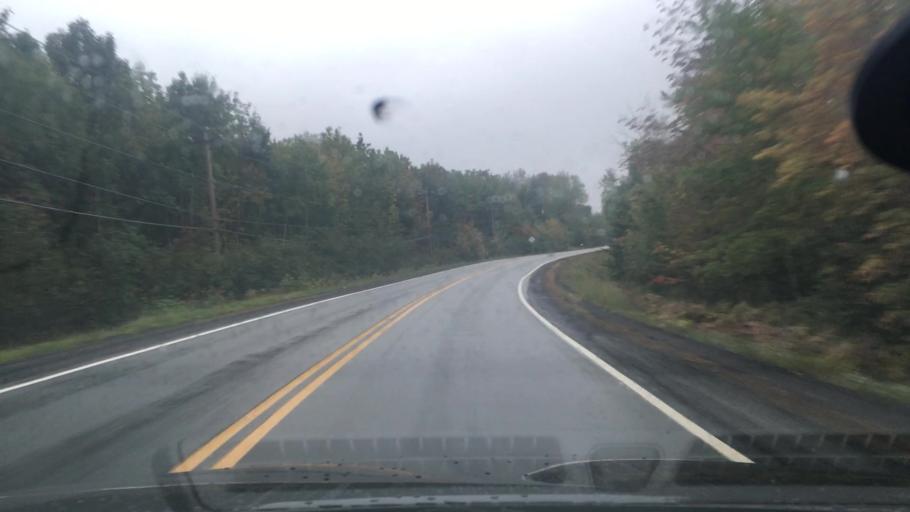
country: CA
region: Nova Scotia
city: Windsor
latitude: 44.8453
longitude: -64.2256
